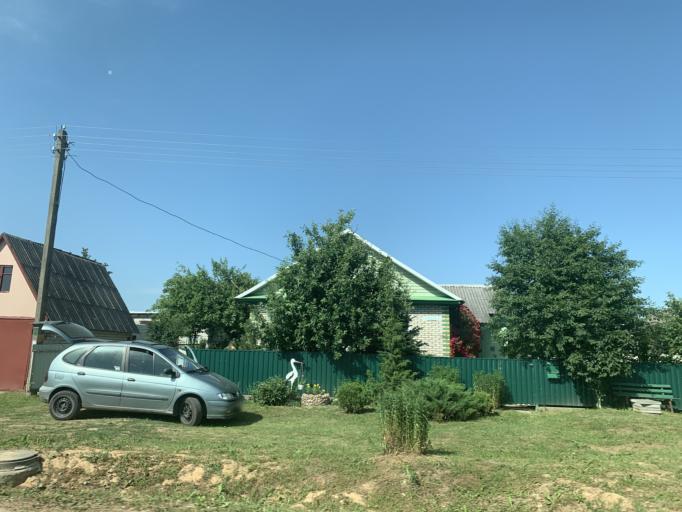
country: BY
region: Minsk
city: Dzyarzhynsk
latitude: 53.6995
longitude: 27.1005
